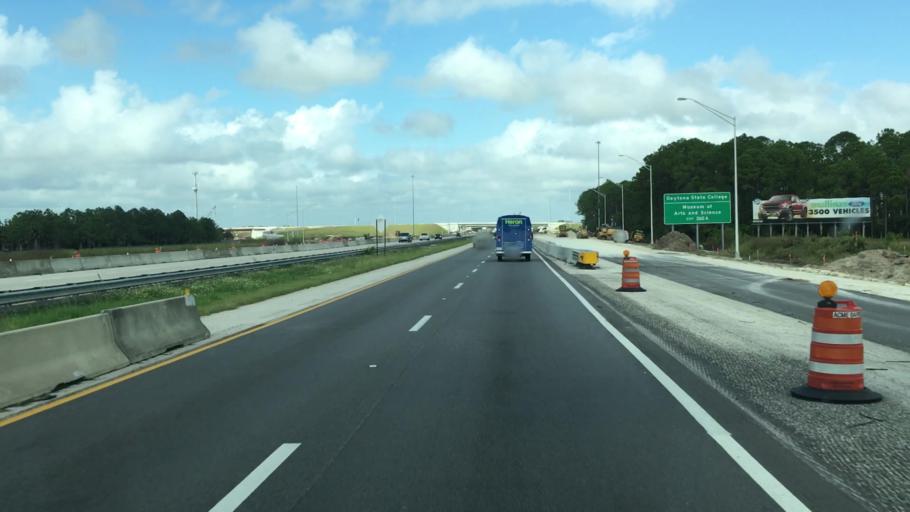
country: US
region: Florida
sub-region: Volusia County
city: South Daytona
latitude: 29.1490
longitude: -81.0719
